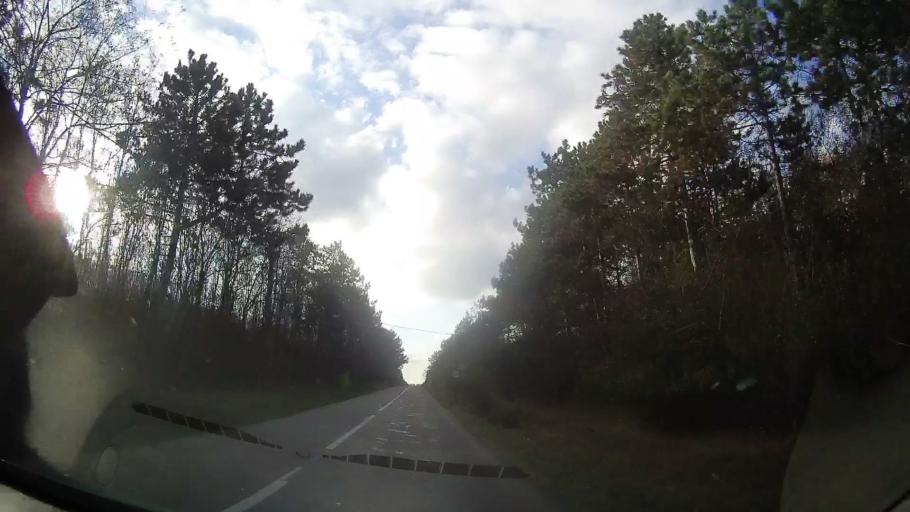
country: RO
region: Constanta
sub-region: Comuna Negru Voda
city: Negru Voda
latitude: 43.8193
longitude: 28.2756
